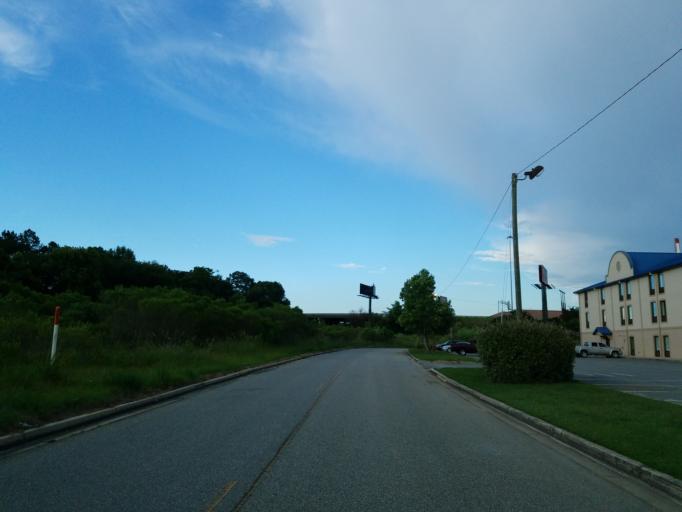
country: US
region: Georgia
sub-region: Tift County
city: Tifton
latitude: 31.4511
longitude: -83.5333
